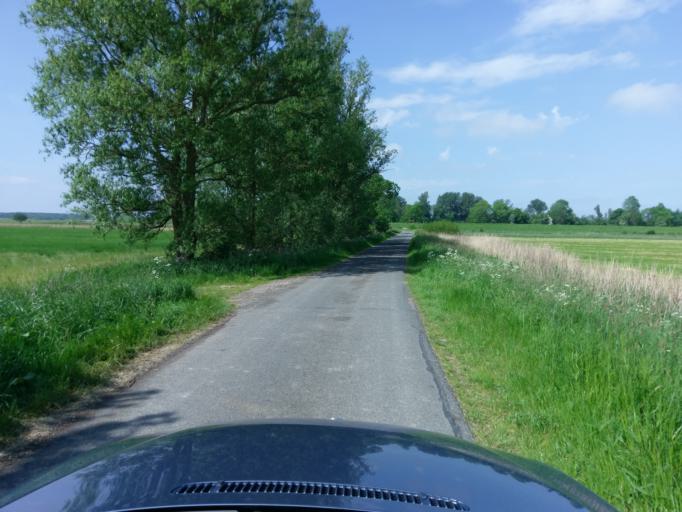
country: DE
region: Schleswig-Holstein
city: Hennstedt
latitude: 54.3193
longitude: 9.1783
